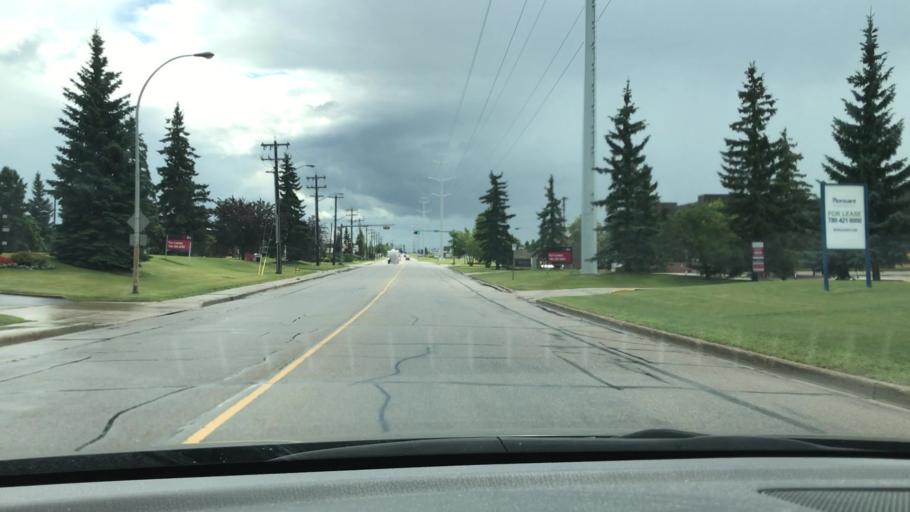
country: CA
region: Alberta
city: Edmonton
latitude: 53.4804
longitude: -113.4792
